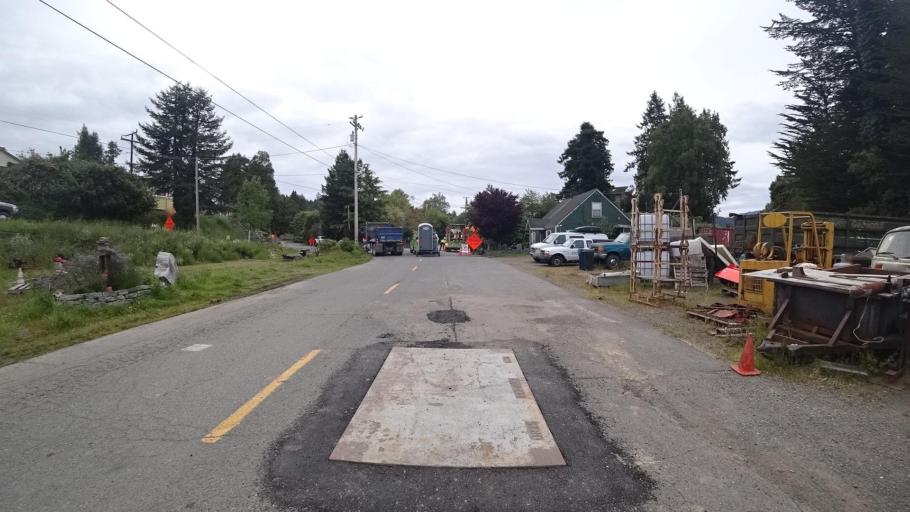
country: US
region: California
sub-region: Humboldt County
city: Blue Lake
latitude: 40.8798
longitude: -123.9879
